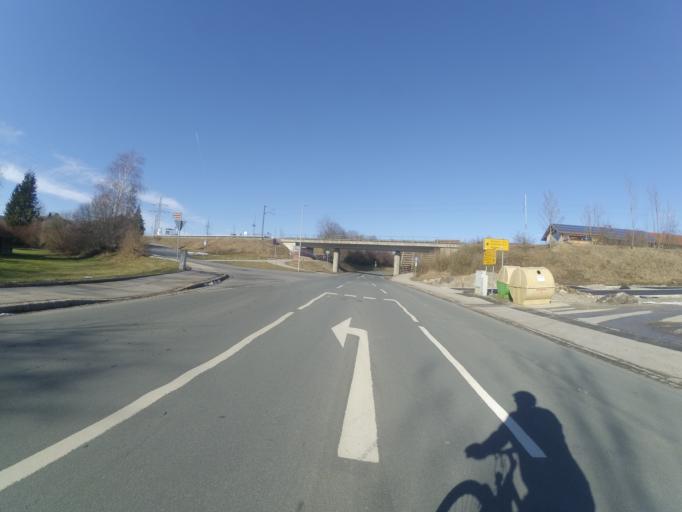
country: DE
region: Bavaria
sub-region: Upper Bavaria
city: Feldkirchen-Westerham
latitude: 47.8946
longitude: 11.8535
